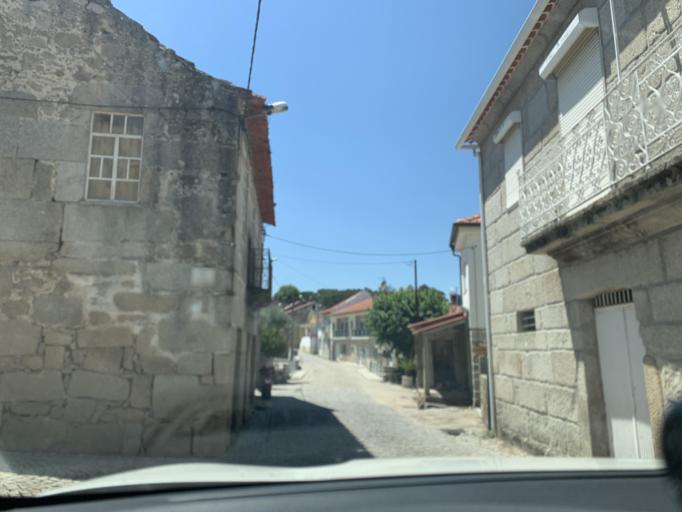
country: PT
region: Viseu
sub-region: Mangualde
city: Mangualde
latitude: 40.5613
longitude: -7.6878
